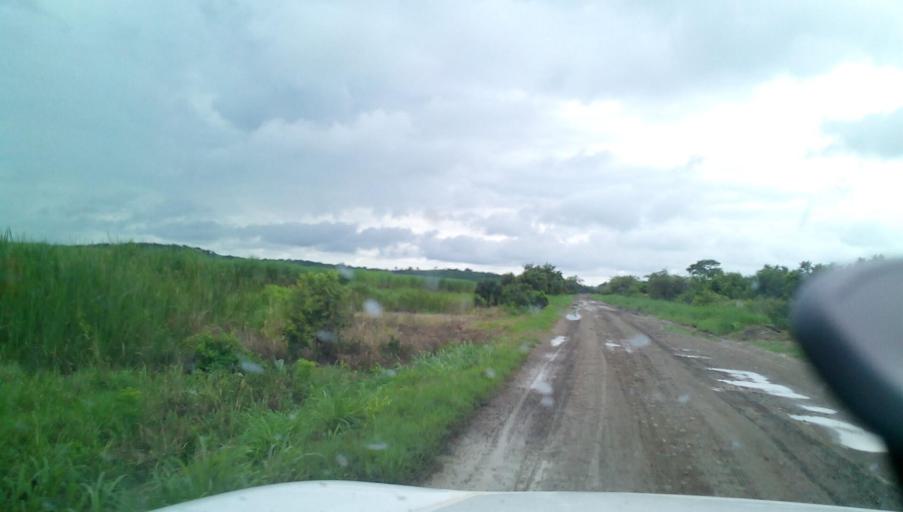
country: MX
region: Veracruz
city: Panuco
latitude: 21.8240
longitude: -98.1108
